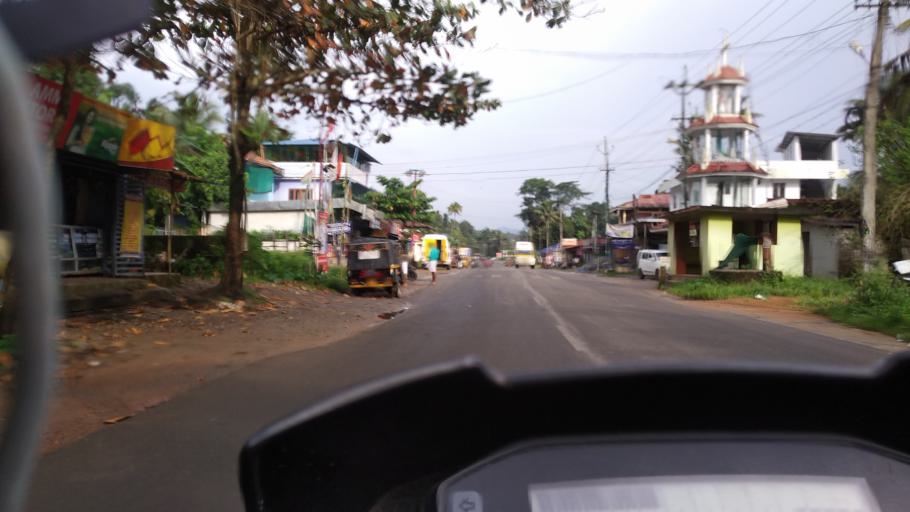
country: IN
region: Kerala
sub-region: Ernakulam
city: Kotamangalam
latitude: 10.0548
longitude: 76.6989
